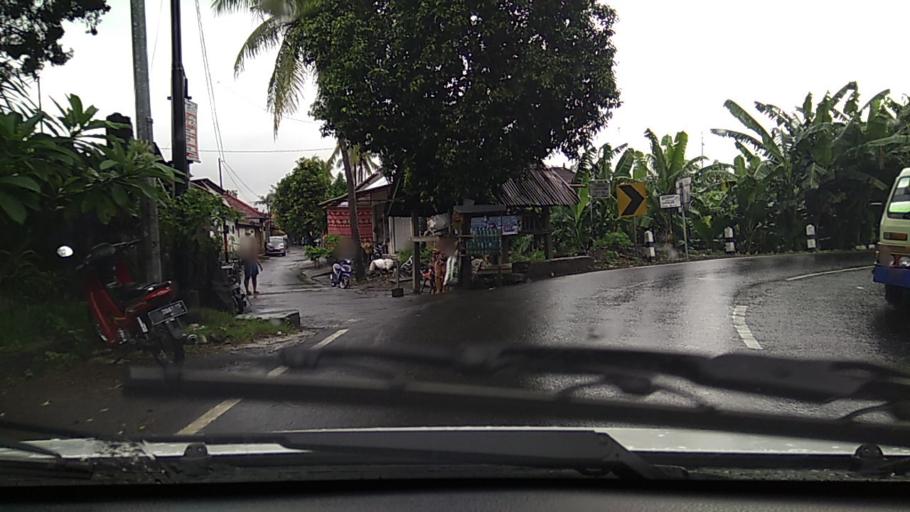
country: ID
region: Bali
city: Banjar Bugbug
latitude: -8.4889
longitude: 115.5954
